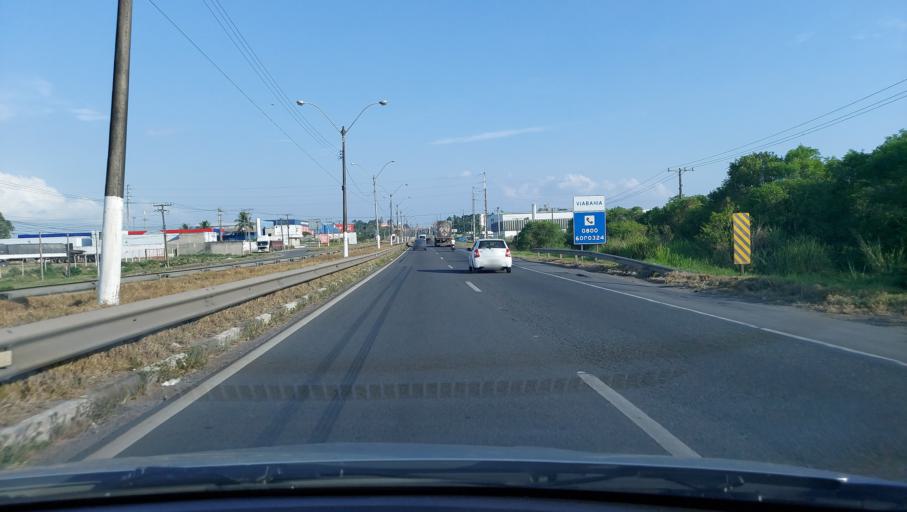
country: BR
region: Bahia
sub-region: Feira De Santana
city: Feira de Santana
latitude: -12.2862
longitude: -38.9171
